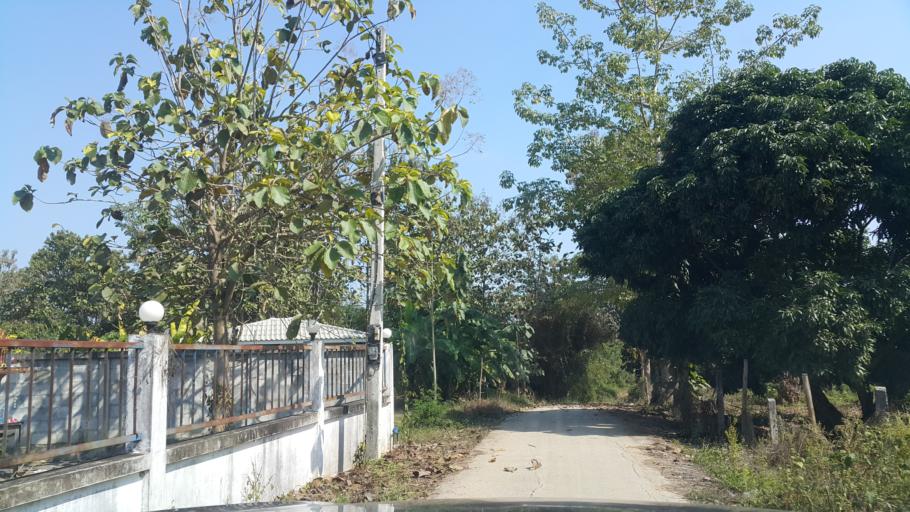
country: TH
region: Sukhothai
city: Thung Saliam
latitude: 17.3209
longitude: 99.5744
